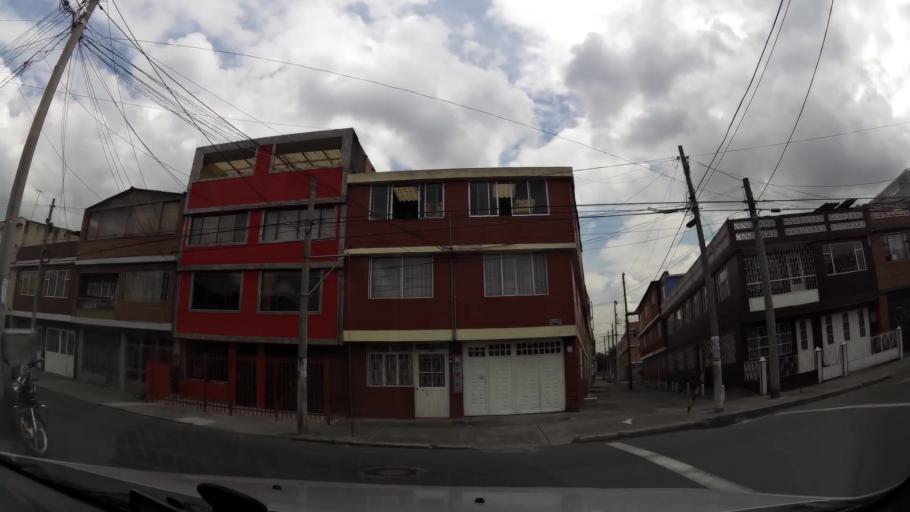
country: CO
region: Bogota D.C.
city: Bogota
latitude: 4.6116
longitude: -74.1152
